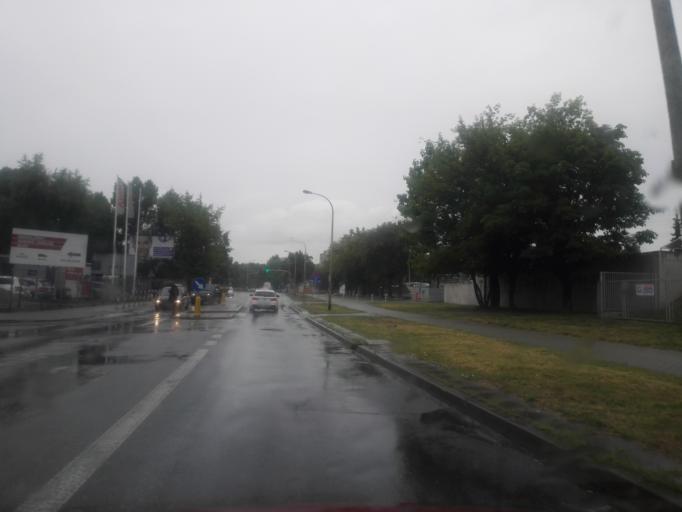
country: PL
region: Masovian Voivodeship
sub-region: Warszawa
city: Mokotow
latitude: 52.1876
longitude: 21.0076
